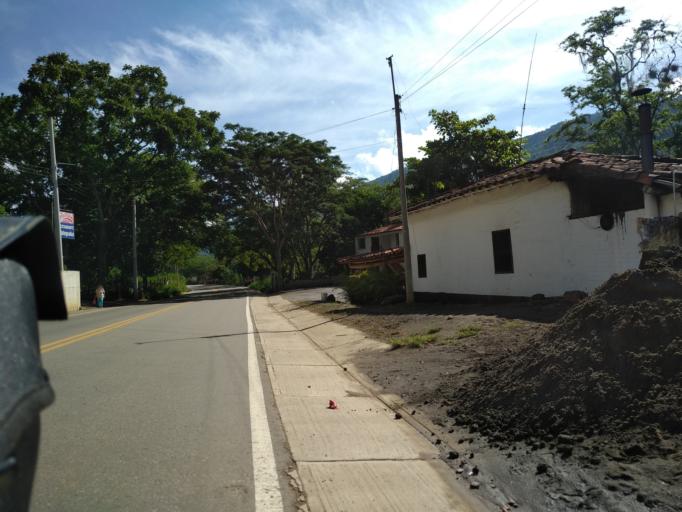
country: CO
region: Santander
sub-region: San Gil
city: San Gil
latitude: 6.5185
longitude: -73.1255
